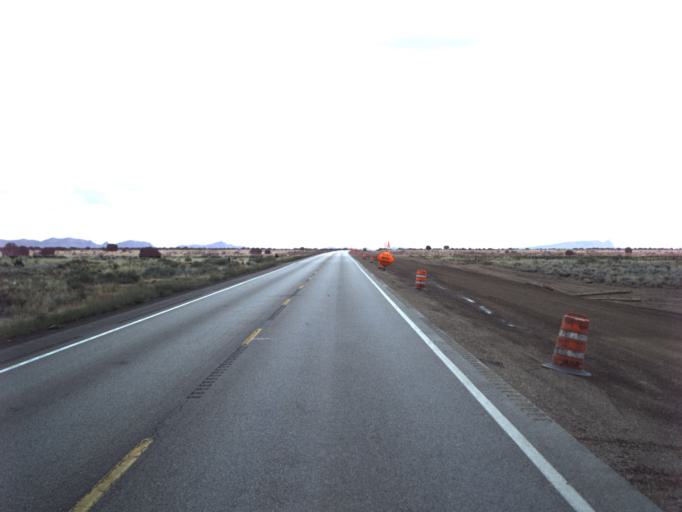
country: US
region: Utah
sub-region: Carbon County
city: East Carbon City
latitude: 39.4308
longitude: -110.4523
